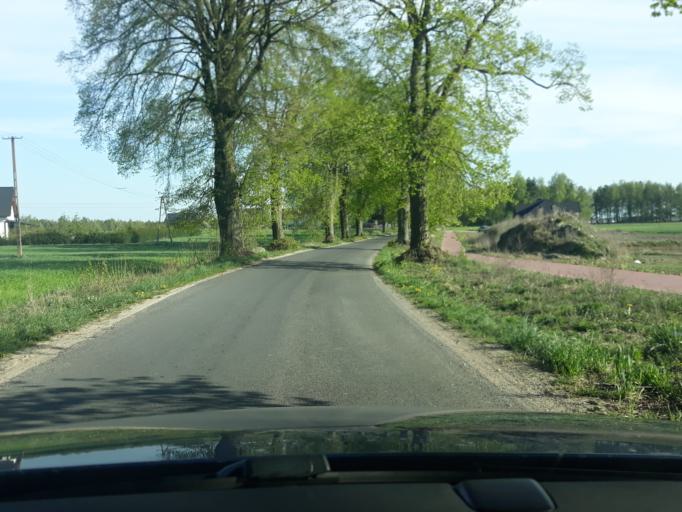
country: PL
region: Pomeranian Voivodeship
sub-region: Powiat czluchowski
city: Przechlewo
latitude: 53.8351
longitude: 17.3672
